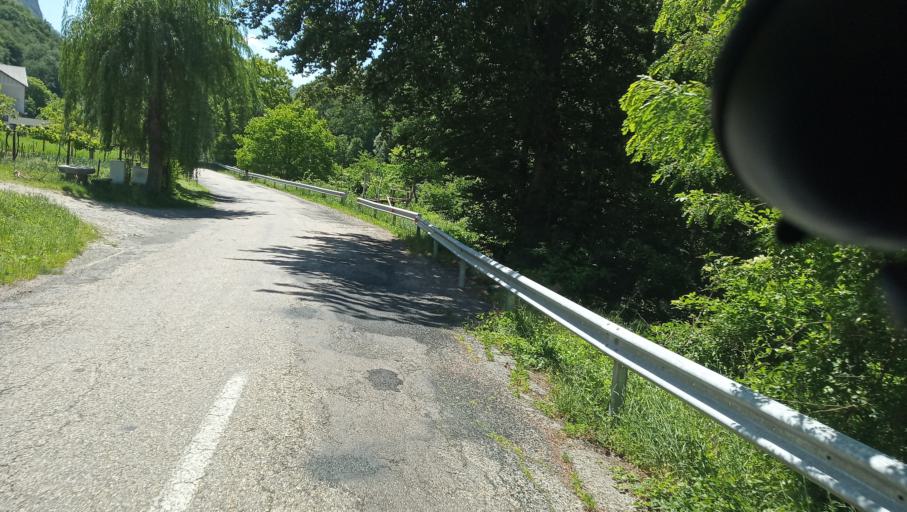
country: RO
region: Caras-Severin
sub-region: Comuna Mehadia
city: Valea Bolvasnita
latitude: 44.9698
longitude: 22.4894
